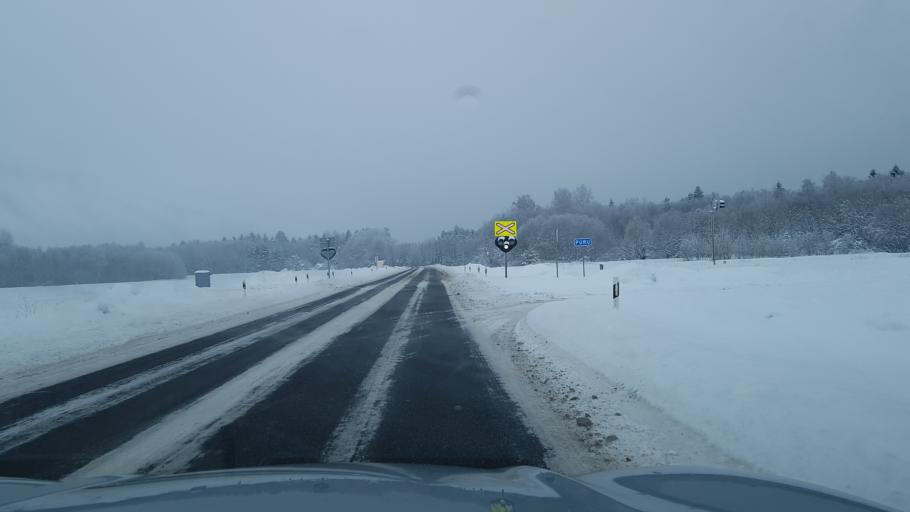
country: EE
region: Ida-Virumaa
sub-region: Johvi vald
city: Johvi
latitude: 59.3108
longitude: 27.3927
